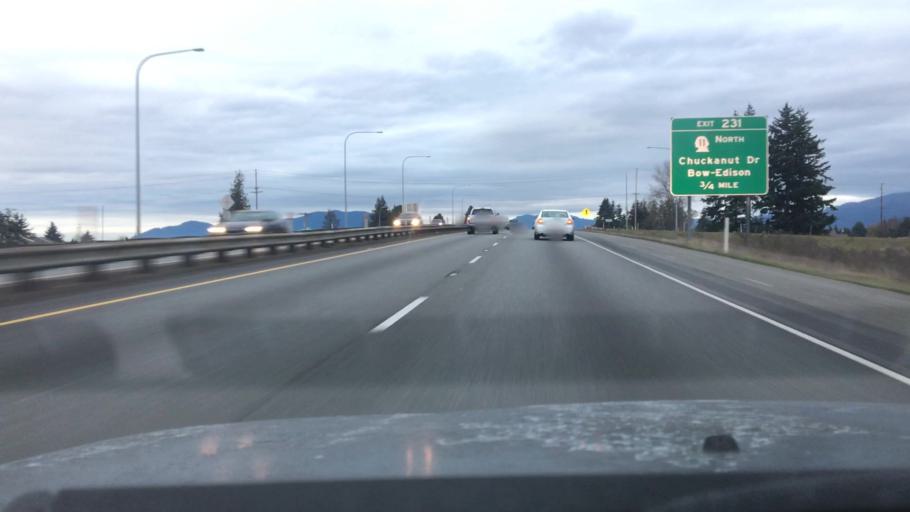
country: US
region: Washington
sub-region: Skagit County
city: Burlington
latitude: 48.4673
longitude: -122.3449
